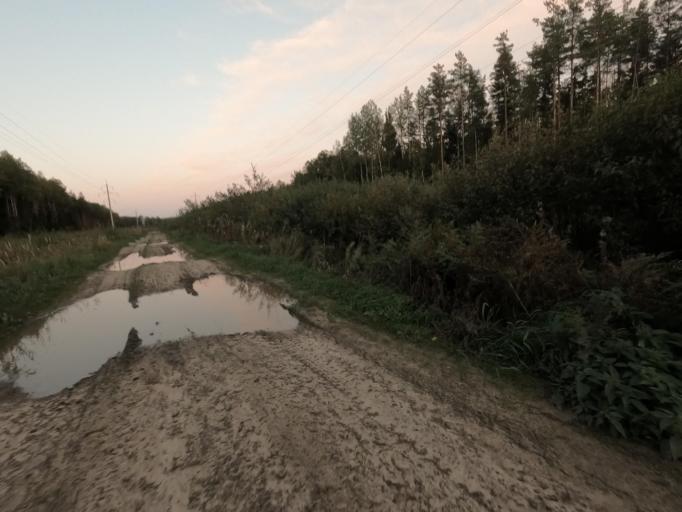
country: RU
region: Leningrad
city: Otradnoye
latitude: 59.7720
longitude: 30.8585
